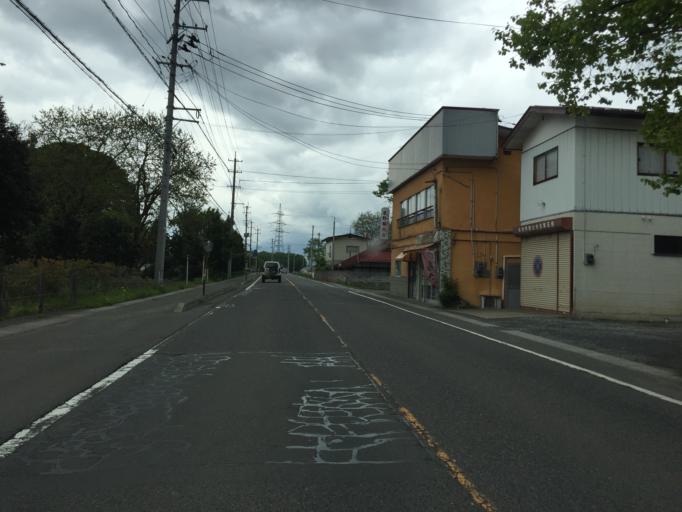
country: JP
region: Fukushima
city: Sukagawa
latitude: 37.1950
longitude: 140.3634
